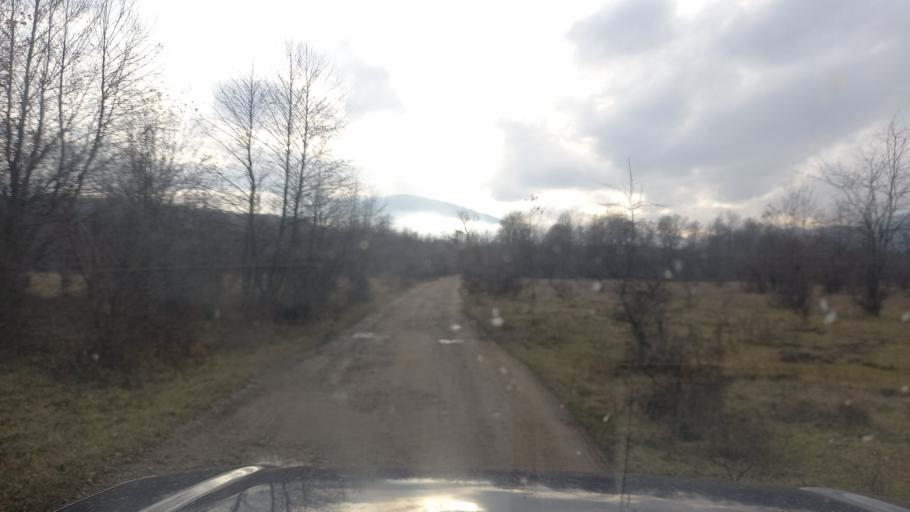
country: RU
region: Krasnodarskiy
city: Neftegorsk
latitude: 44.2426
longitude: 39.7633
